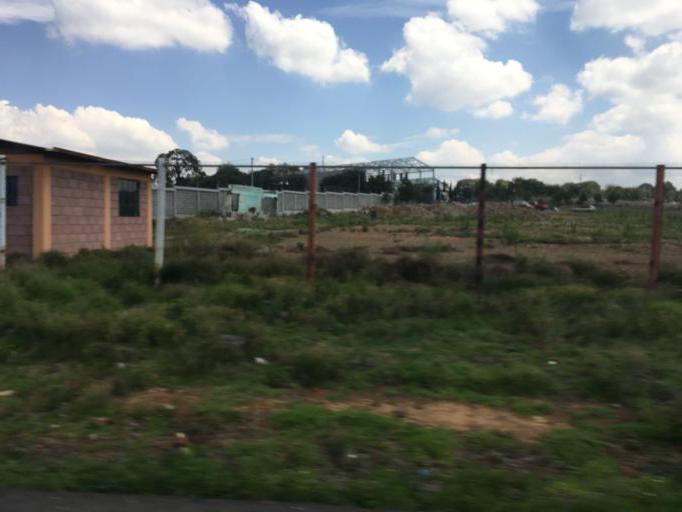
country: MX
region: Mexico
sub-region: Jilotepec
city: Octeyuco Dos Mil
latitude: 19.8885
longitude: -99.6401
